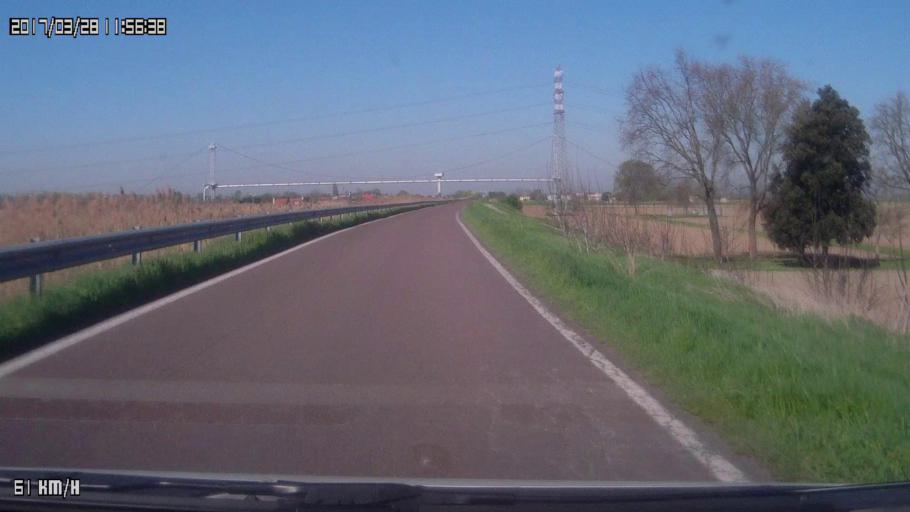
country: IT
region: Veneto
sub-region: Provincia di Venezia
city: Boscochiaro
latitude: 45.1338
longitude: 12.1359
